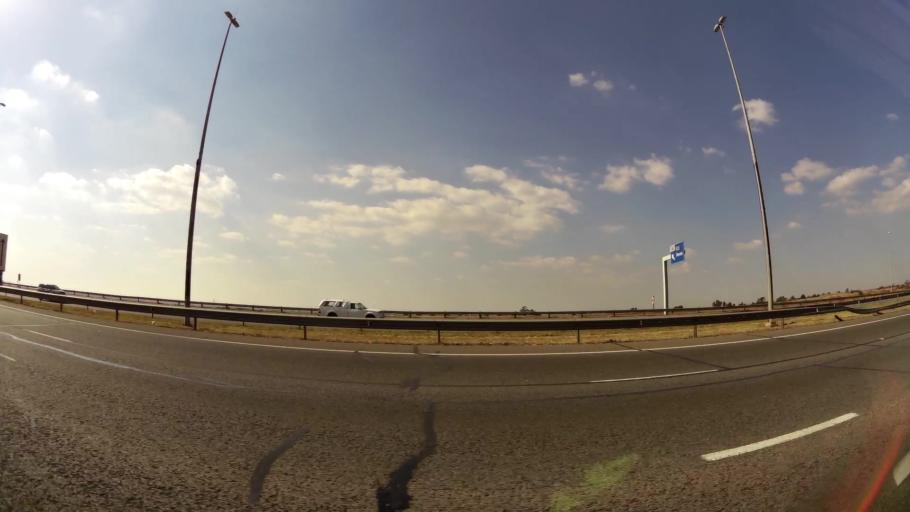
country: ZA
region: Gauteng
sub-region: Ekurhuleni Metropolitan Municipality
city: Tembisa
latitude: -26.0570
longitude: 28.2805
